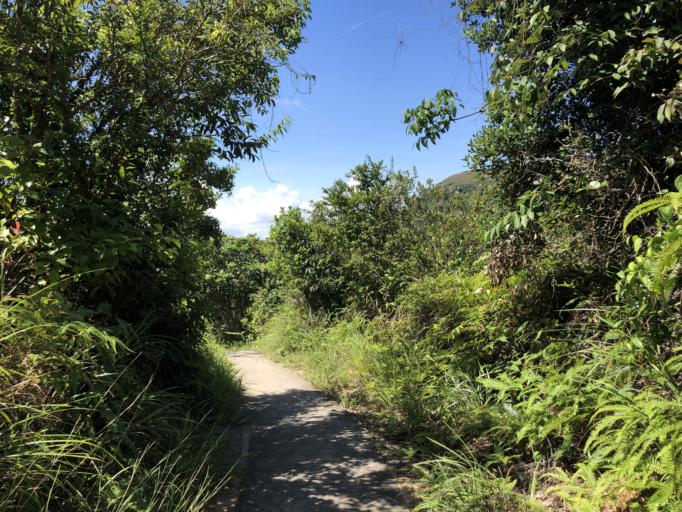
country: HK
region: Tuen Mun
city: Tuen Mun
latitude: 22.2849
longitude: 113.9819
